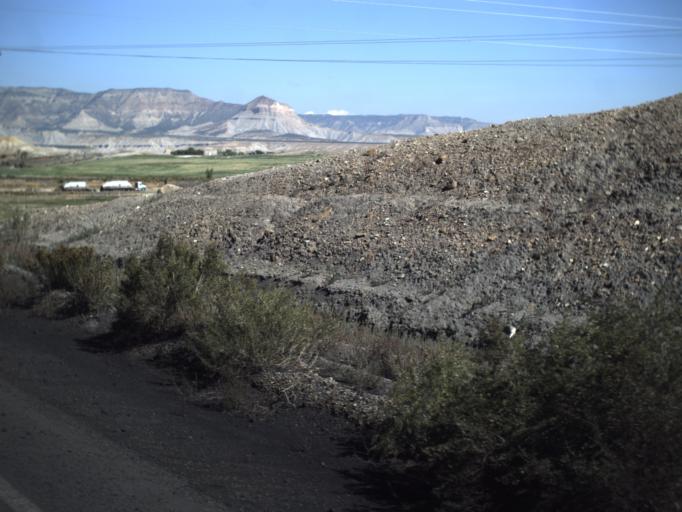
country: US
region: Utah
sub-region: Emery County
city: Castle Dale
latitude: 39.1732
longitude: -111.0446
